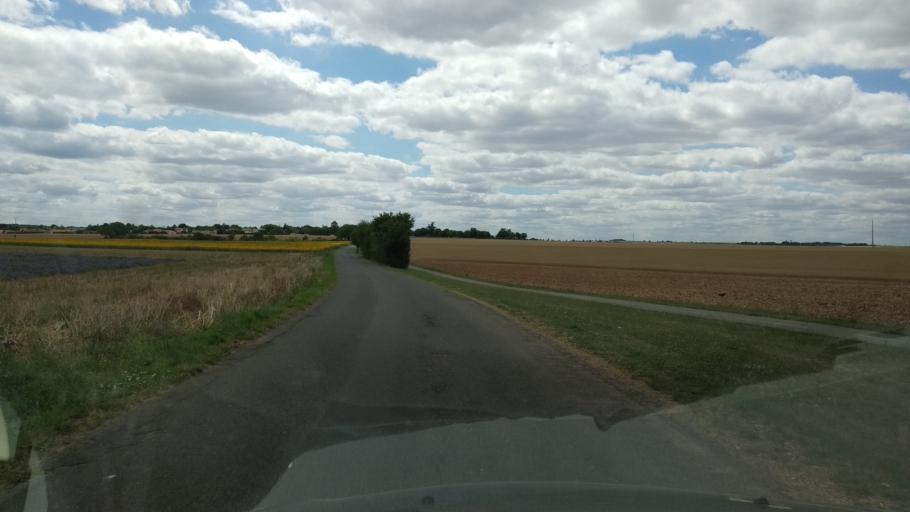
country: FR
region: Poitou-Charentes
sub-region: Departement de la Vienne
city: Avanton
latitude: 46.6706
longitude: 0.3206
